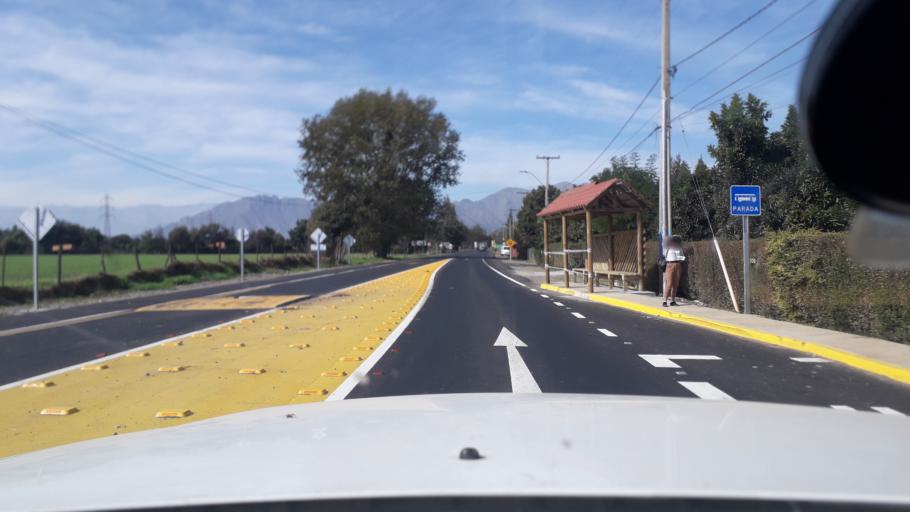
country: CL
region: Valparaiso
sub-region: Provincia de San Felipe
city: Llaillay
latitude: -32.8034
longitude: -70.9036
